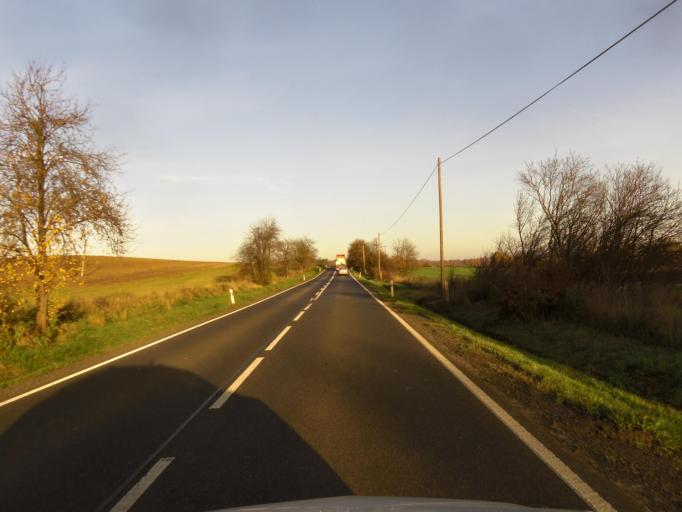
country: CZ
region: Liberecky
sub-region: Okres Ceska Lipa
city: Ceska Lipa
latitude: 50.6354
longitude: 14.4866
